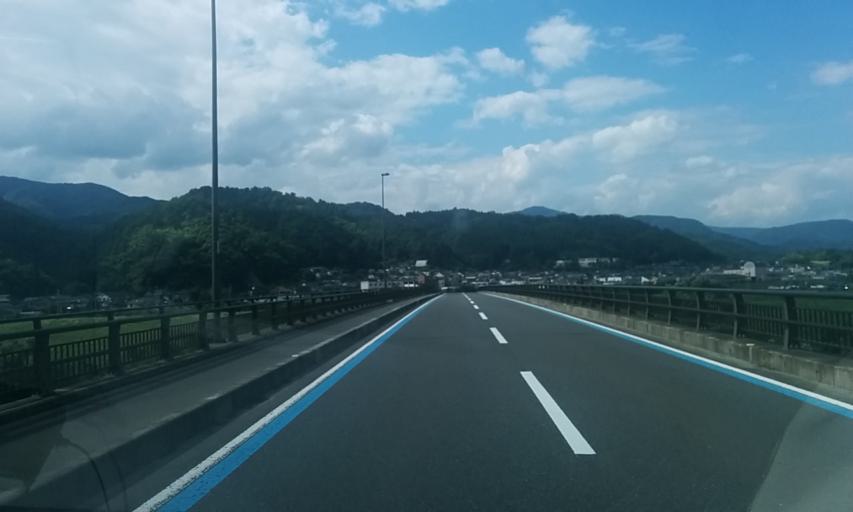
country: JP
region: Kyoto
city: Fukuchiyama
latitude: 35.3829
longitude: 135.1478
